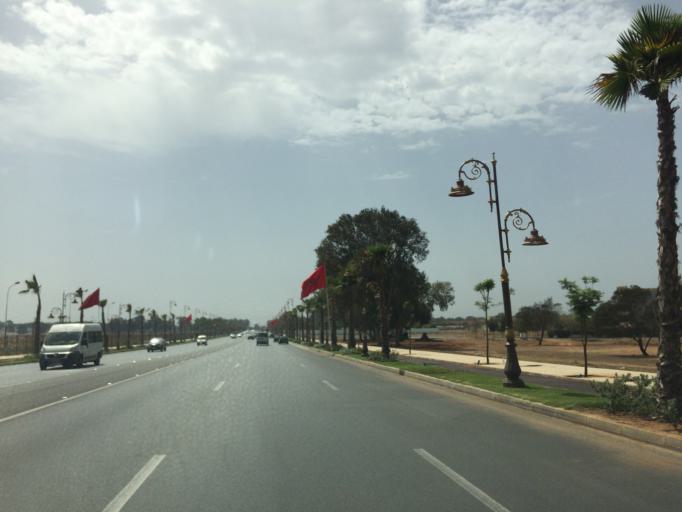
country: MA
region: Rabat-Sale-Zemmour-Zaer
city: Sale
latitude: 34.0323
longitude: -6.7670
